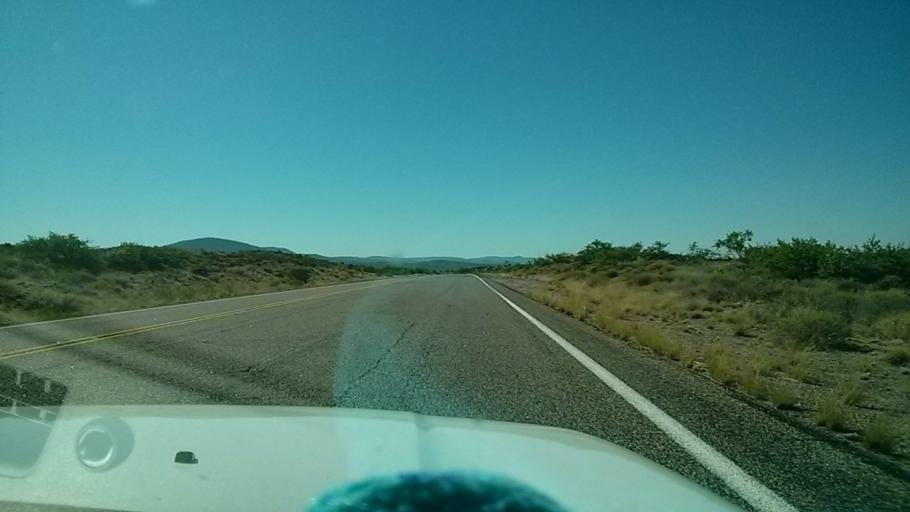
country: US
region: Arizona
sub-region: Mohave County
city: New Kingman-Butler
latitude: 35.3716
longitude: -113.7189
